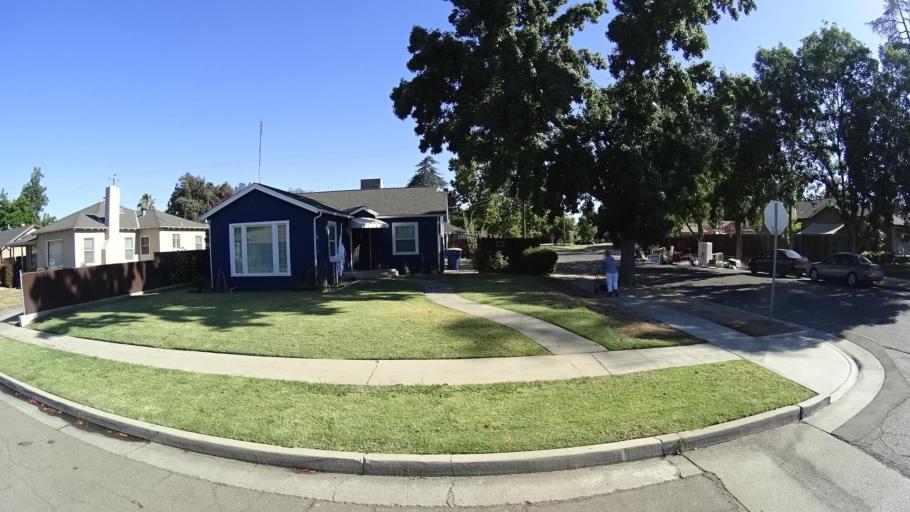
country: US
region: California
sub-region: Fresno County
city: Fresno
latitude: 36.7714
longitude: -119.7884
